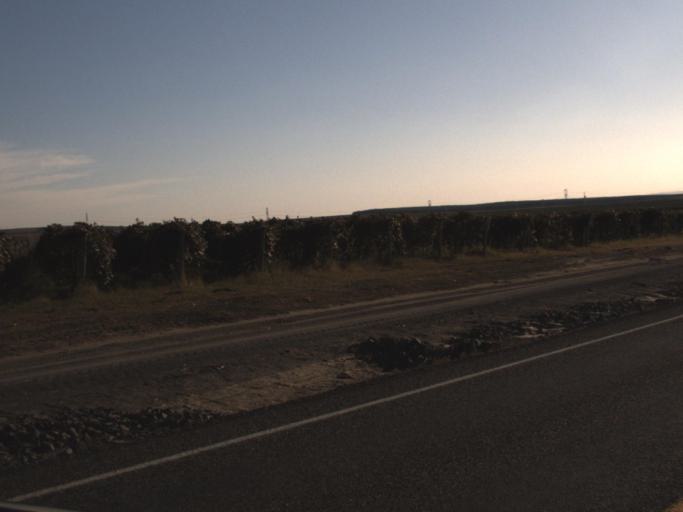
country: US
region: Washington
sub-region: Walla Walla County
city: Burbank
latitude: 46.2300
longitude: -118.8487
